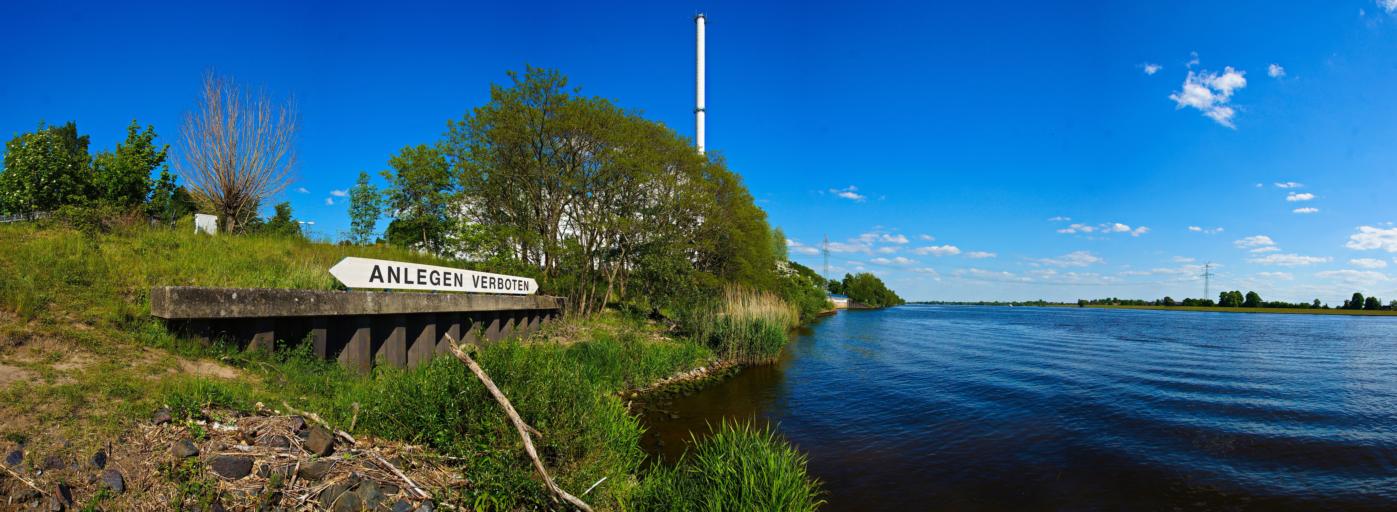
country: DE
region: Lower Saxony
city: Tespe
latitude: 53.4110
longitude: 10.4051
